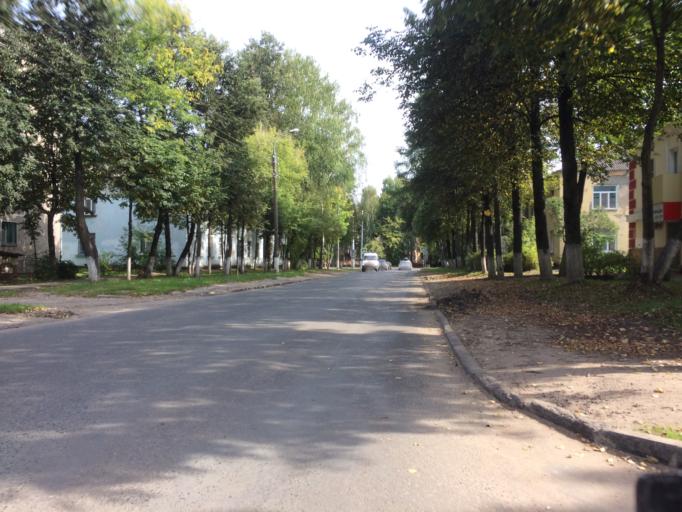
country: RU
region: Mariy-El
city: Yoshkar-Ola
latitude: 56.6298
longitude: 47.8787
